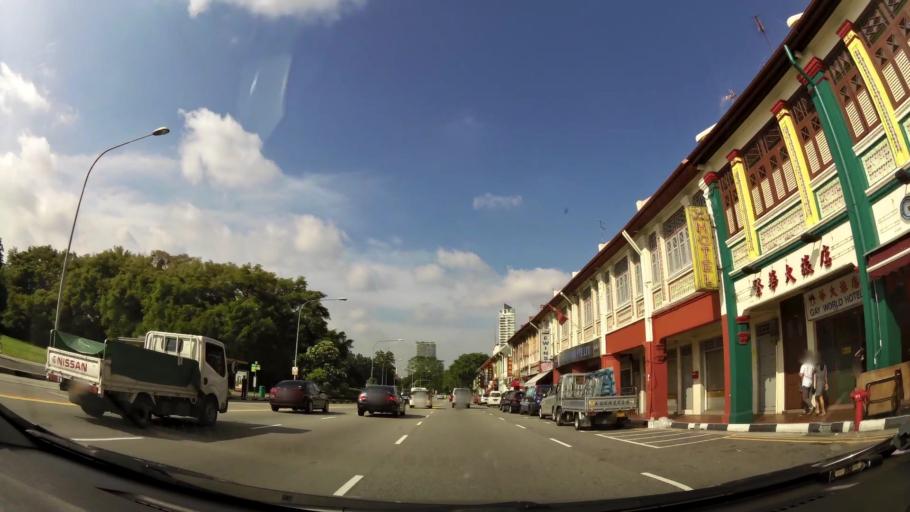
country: SG
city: Singapore
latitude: 1.3110
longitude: 103.8738
